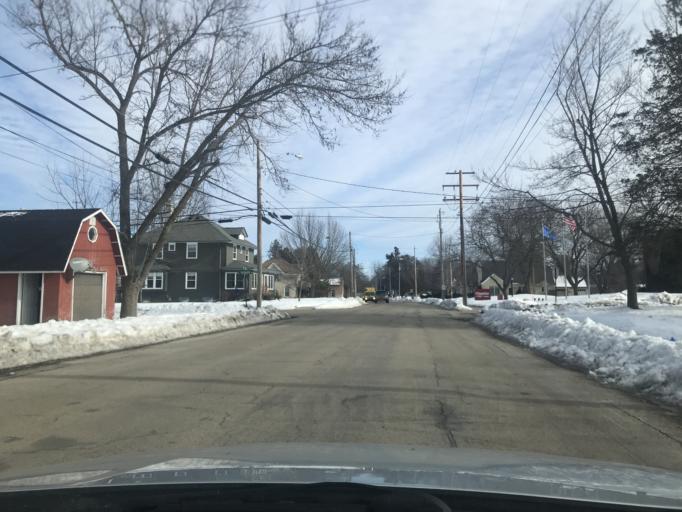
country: US
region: Wisconsin
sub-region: Oconto County
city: Gillett
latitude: 44.8893
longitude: -88.3080
